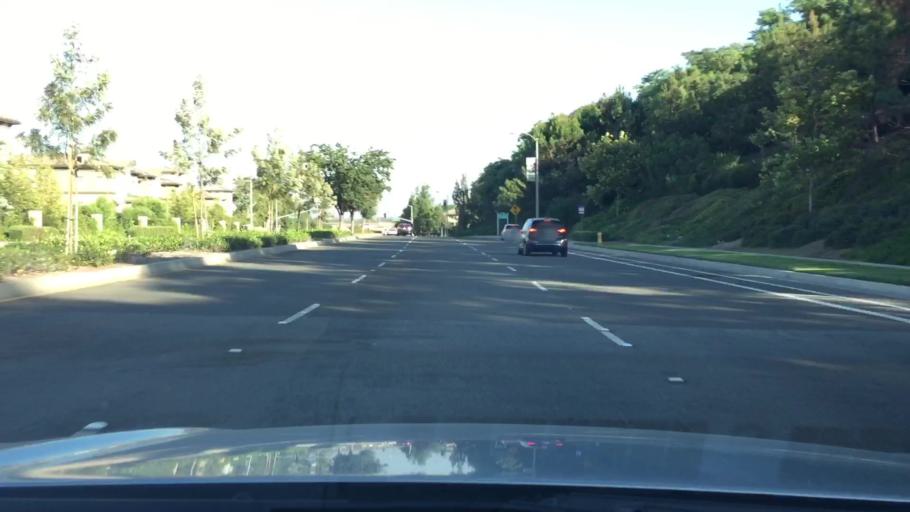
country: US
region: California
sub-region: San Bernardino County
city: Los Serranos
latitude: 33.9553
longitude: -117.6880
